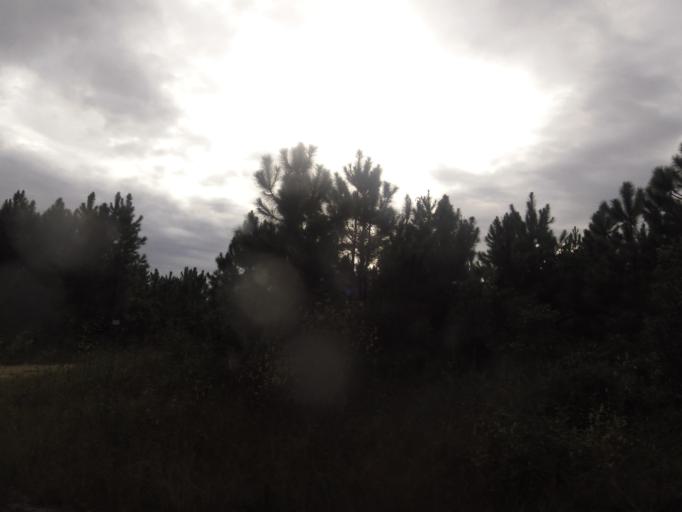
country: US
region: Florida
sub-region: Flagler County
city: Bunnell
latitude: 29.5573
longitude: -81.3312
